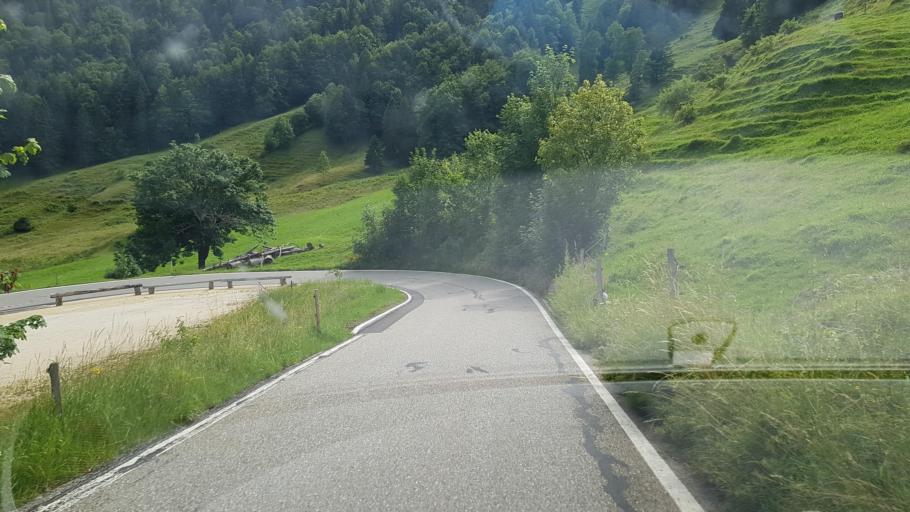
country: CH
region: Solothurn
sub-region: Bezirk Thal
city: Welschenrohr
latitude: 47.2626
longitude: 7.5401
